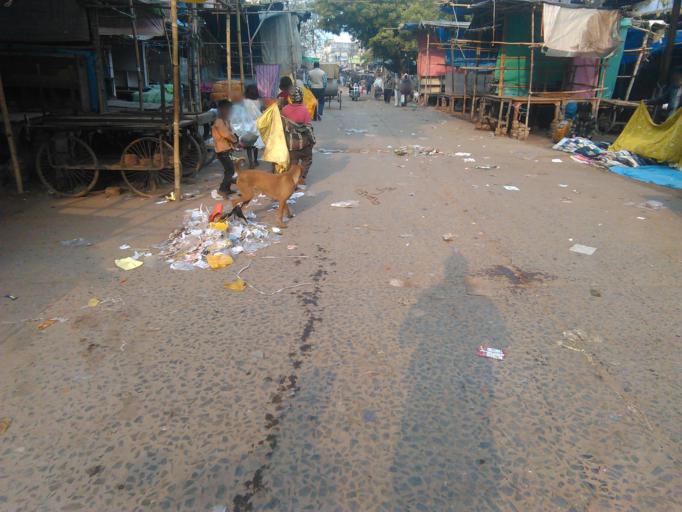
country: IN
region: Bihar
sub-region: Gaya
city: Gaya
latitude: 24.7972
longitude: 85.0070
